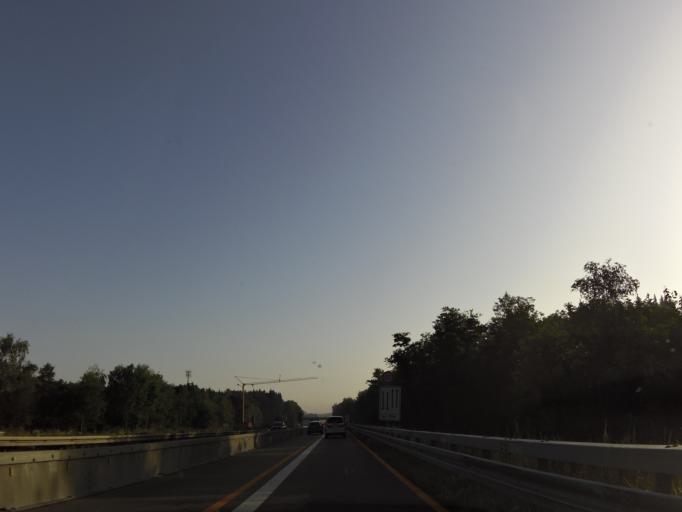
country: DE
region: Bavaria
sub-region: Swabia
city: Holzheim
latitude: 48.3699
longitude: 10.0835
